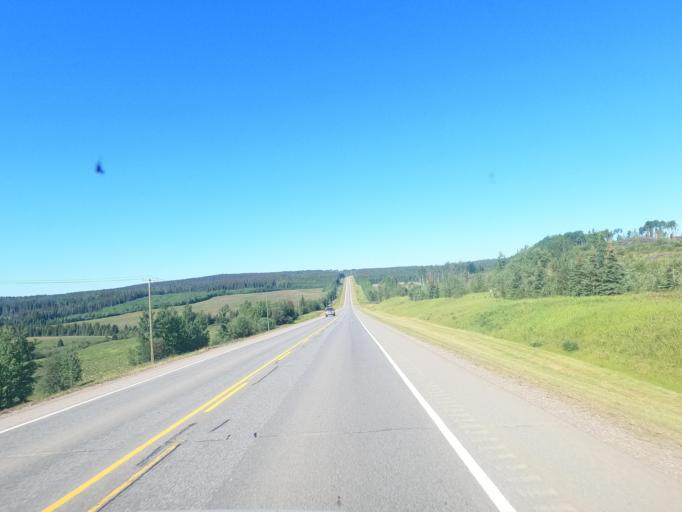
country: CA
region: British Columbia
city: Fort St. John
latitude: 56.6297
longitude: -121.5335
